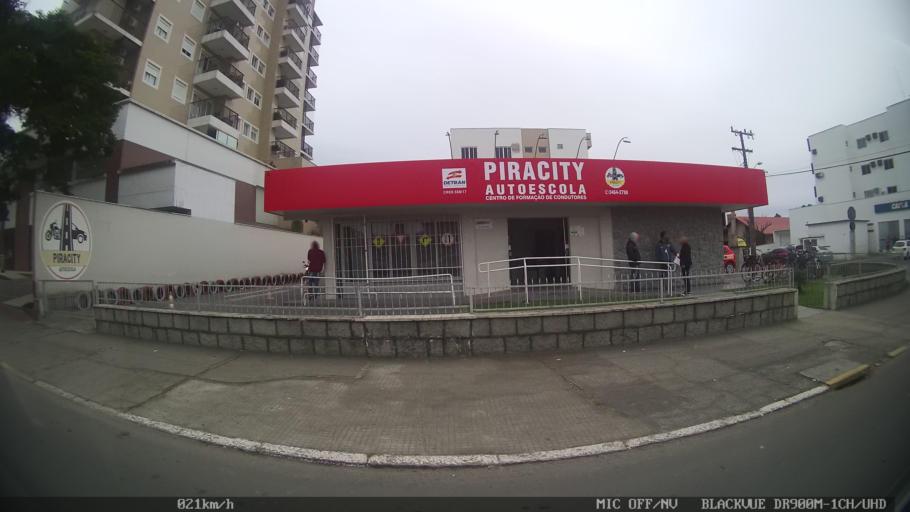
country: BR
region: Santa Catarina
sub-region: Joinville
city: Joinville
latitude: -26.2058
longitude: -48.9088
